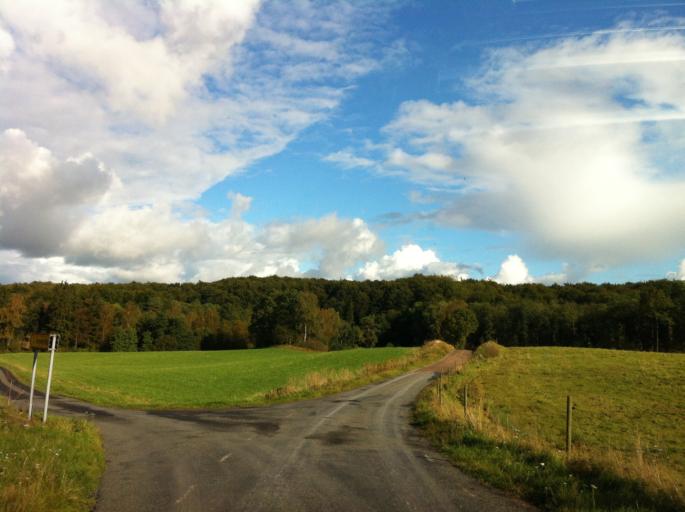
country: SE
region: Skane
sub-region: Perstorps Kommun
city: Perstorp
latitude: 56.1384
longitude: 13.5323
